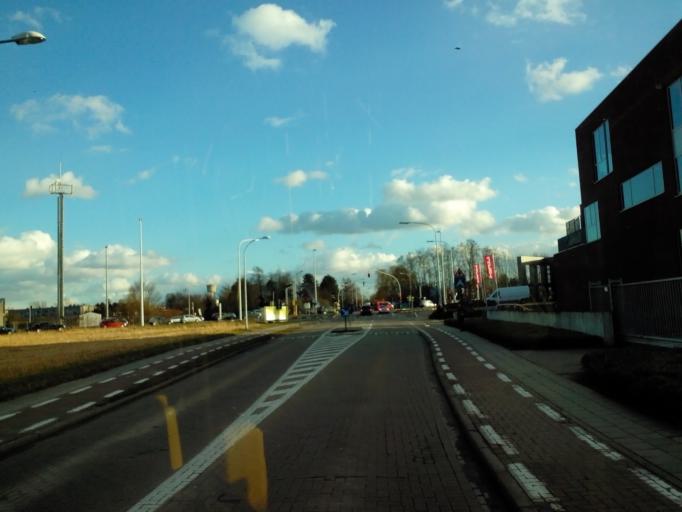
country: BE
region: Flanders
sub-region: Provincie Vlaams-Brabant
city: Leuven
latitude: 50.8521
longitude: 4.7216
